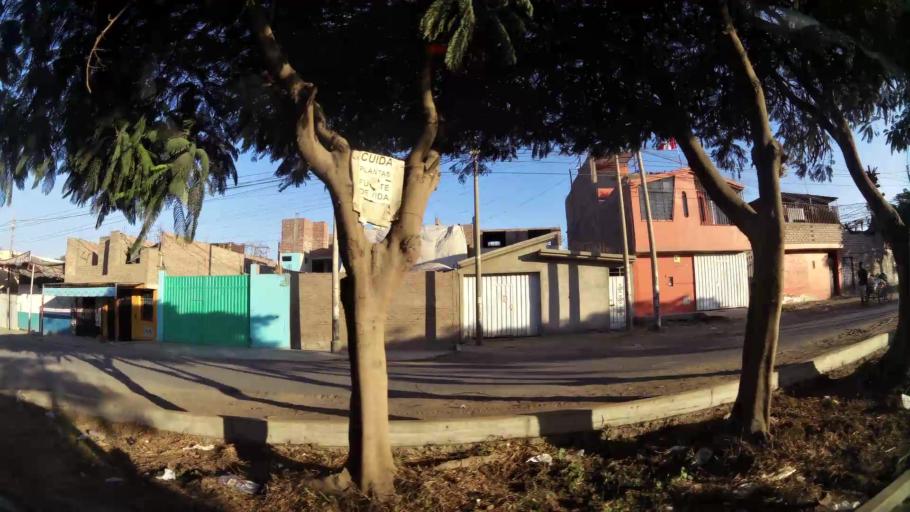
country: PE
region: Ica
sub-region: Provincia de Ica
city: Ica
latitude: -14.0564
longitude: -75.7326
